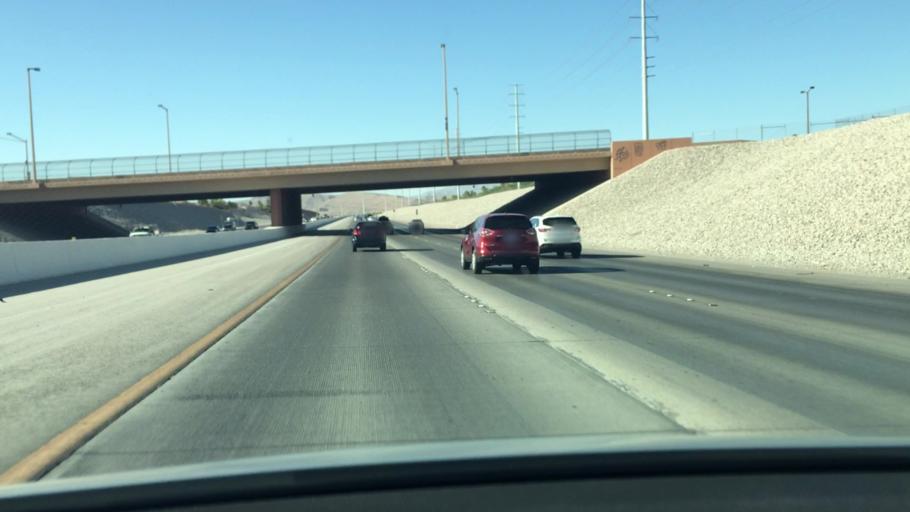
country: US
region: Nevada
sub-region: Clark County
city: Summerlin South
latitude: 36.1456
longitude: -115.3369
